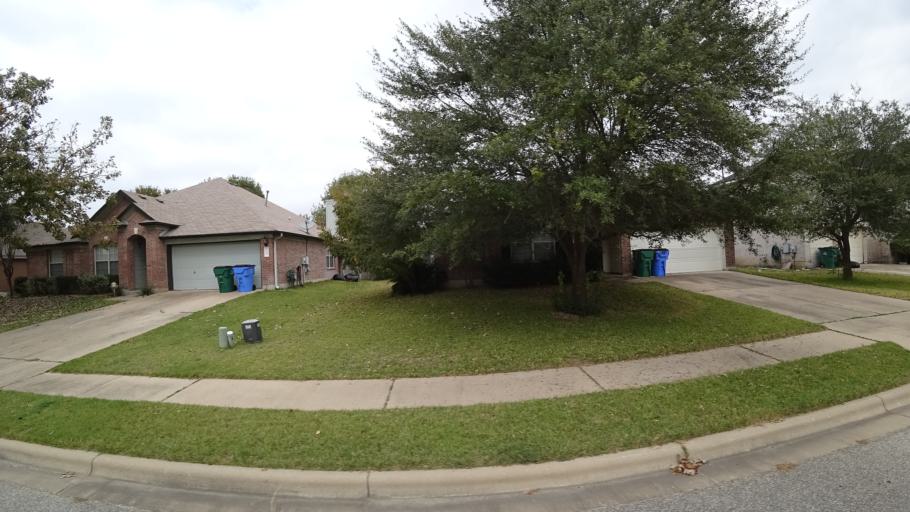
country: US
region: Texas
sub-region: Travis County
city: Pflugerville
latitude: 30.4383
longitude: -97.6062
